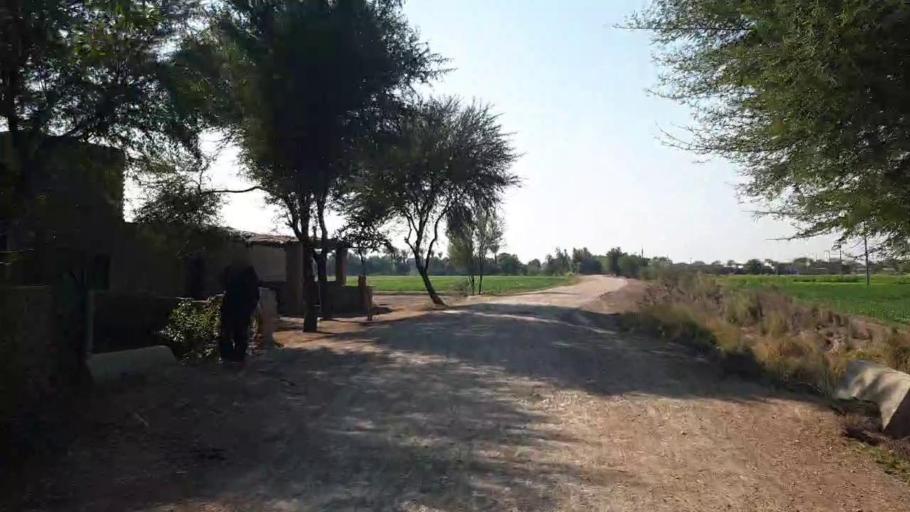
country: PK
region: Sindh
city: Shahdadpur
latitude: 25.9641
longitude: 68.6458
